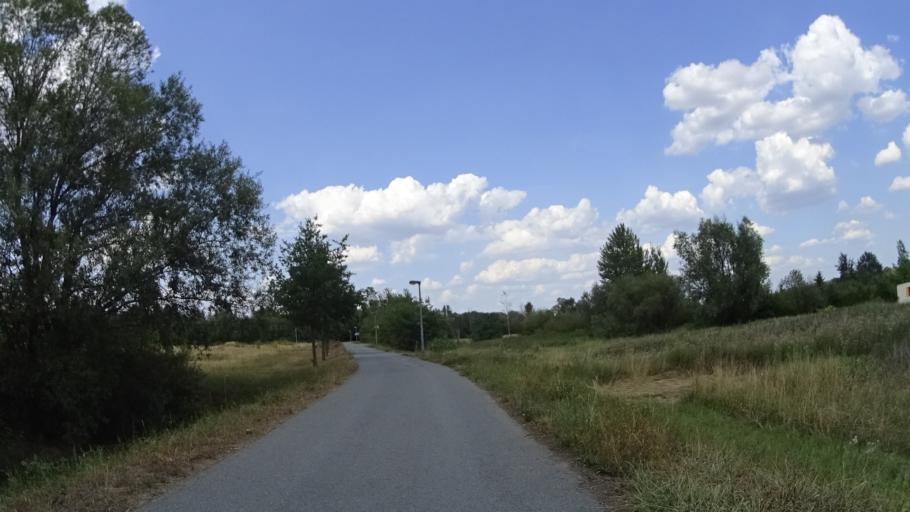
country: DE
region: Saxony
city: Ostritz
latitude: 51.0214
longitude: 14.9324
